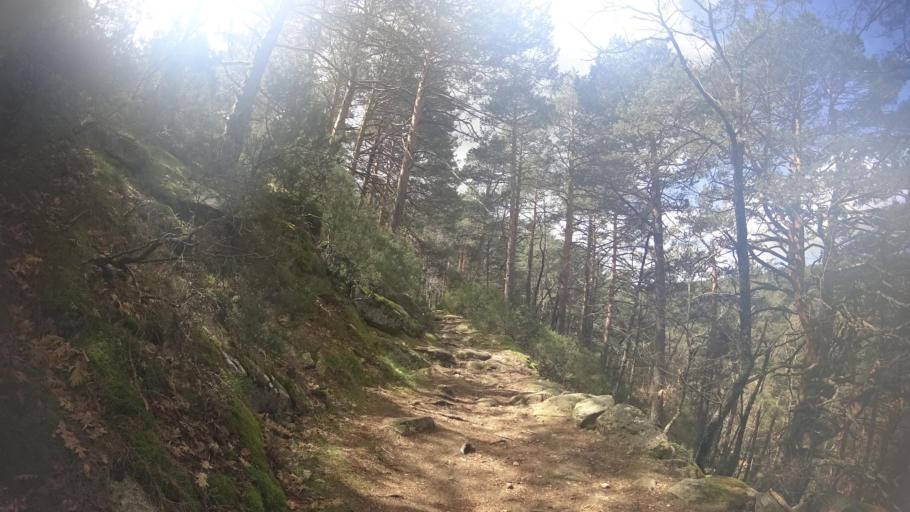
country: ES
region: Madrid
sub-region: Provincia de Madrid
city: Canencia
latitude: 40.8724
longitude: -3.7794
